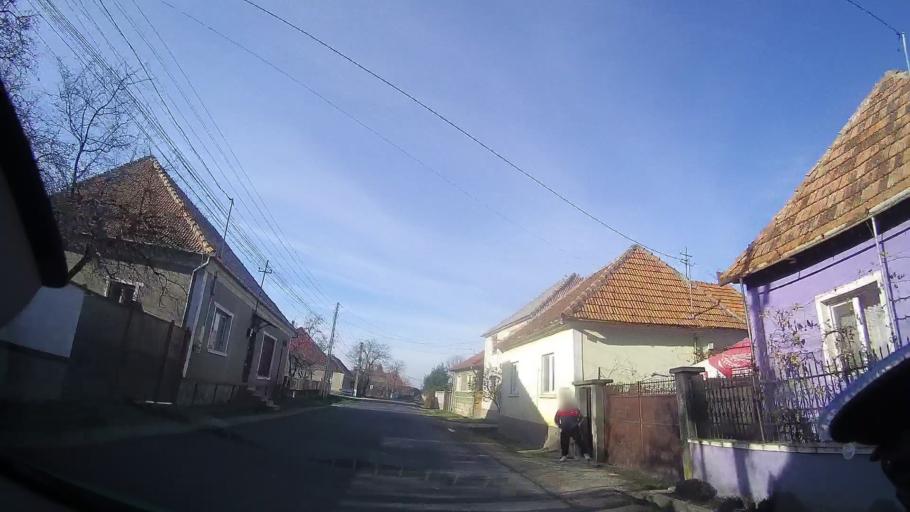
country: RO
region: Bihor
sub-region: Comuna Magesti
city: Magesti
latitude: 47.0121
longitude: 22.4451
